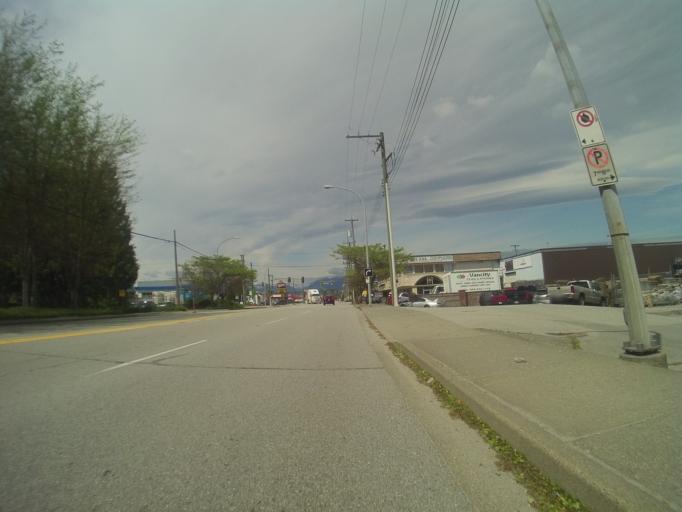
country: CA
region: British Columbia
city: Richmond
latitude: 49.1910
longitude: -123.0914
